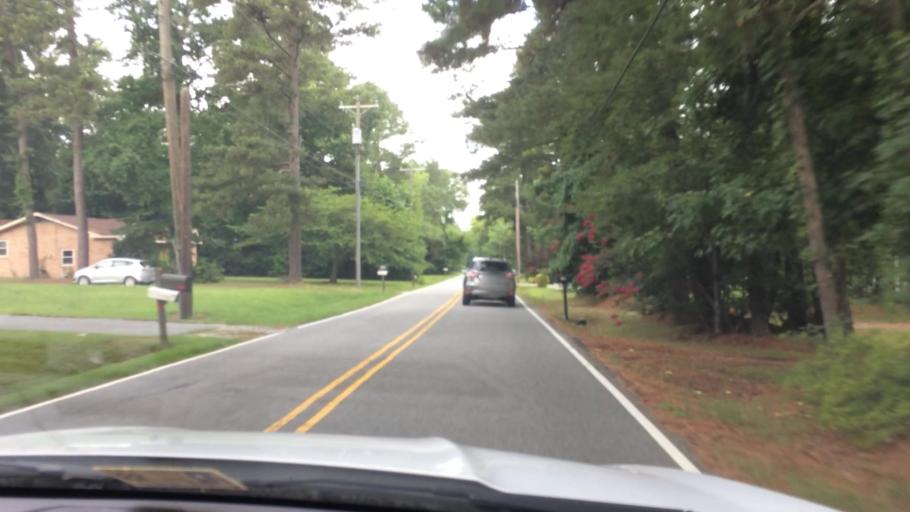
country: US
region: Virginia
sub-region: City of Poquoson
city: Poquoson
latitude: 37.1444
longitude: -76.4470
